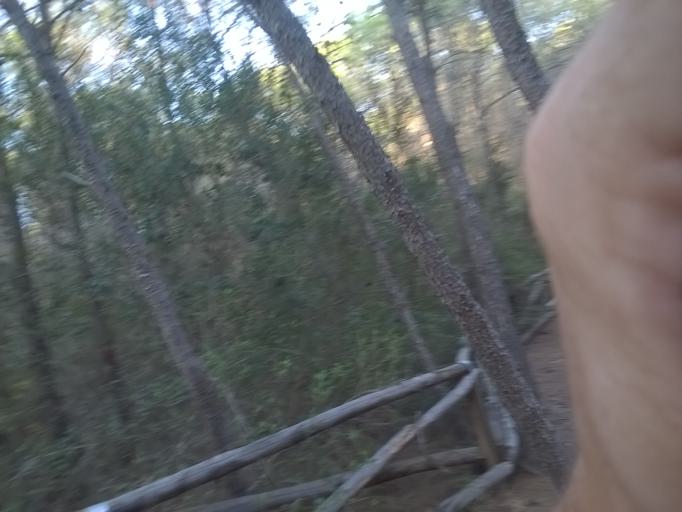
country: IT
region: Apulia
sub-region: Provincia di Taranto
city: Marina di Ginosa
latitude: 40.4711
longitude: 16.9445
